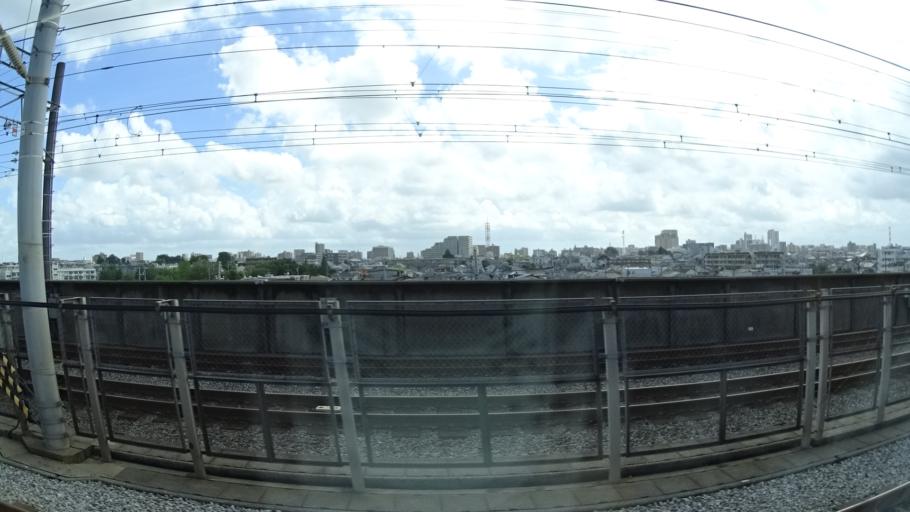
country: JP
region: Saitama
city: Yono
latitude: 35.8661
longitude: 139.6315
